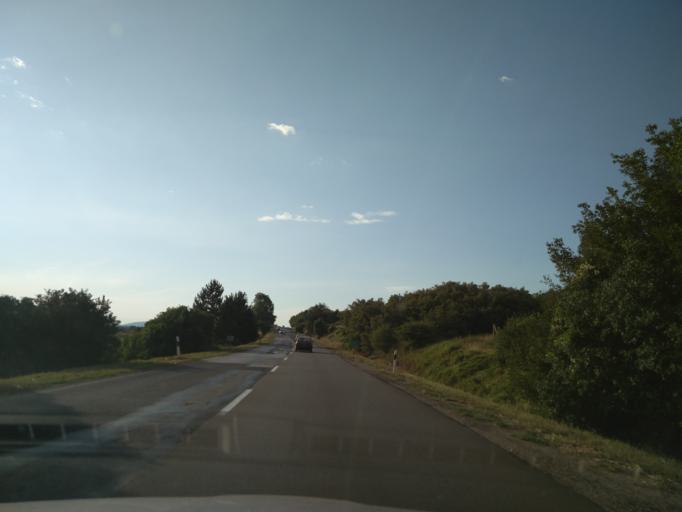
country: HU
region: Veszprem
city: Veszprem
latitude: 47.0977
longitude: 17.8736
